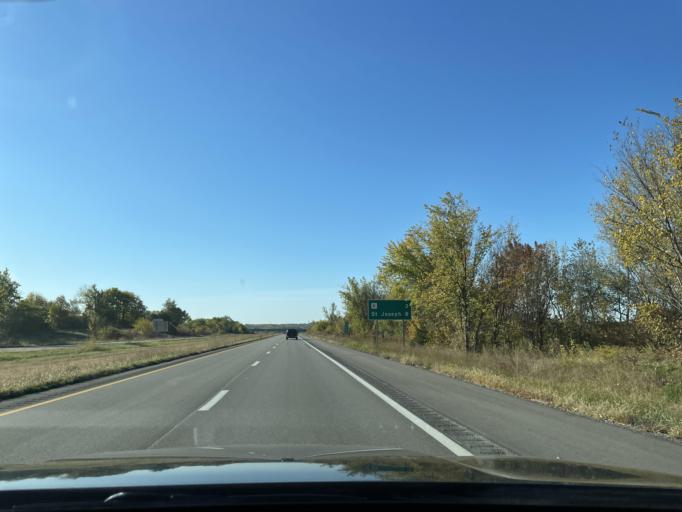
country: US
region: Missouri
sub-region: Andrew County
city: Country Club Village
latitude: 39.8776
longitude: -94.8573
